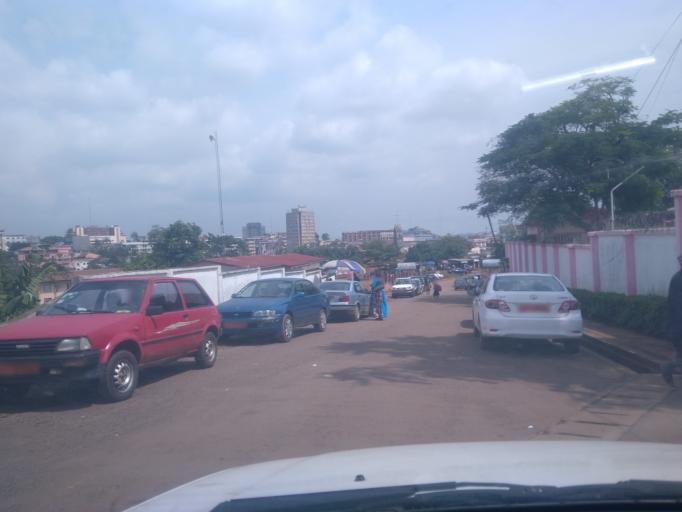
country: CM
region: Centre
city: Yaounde
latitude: 3.8706
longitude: 11.5119
